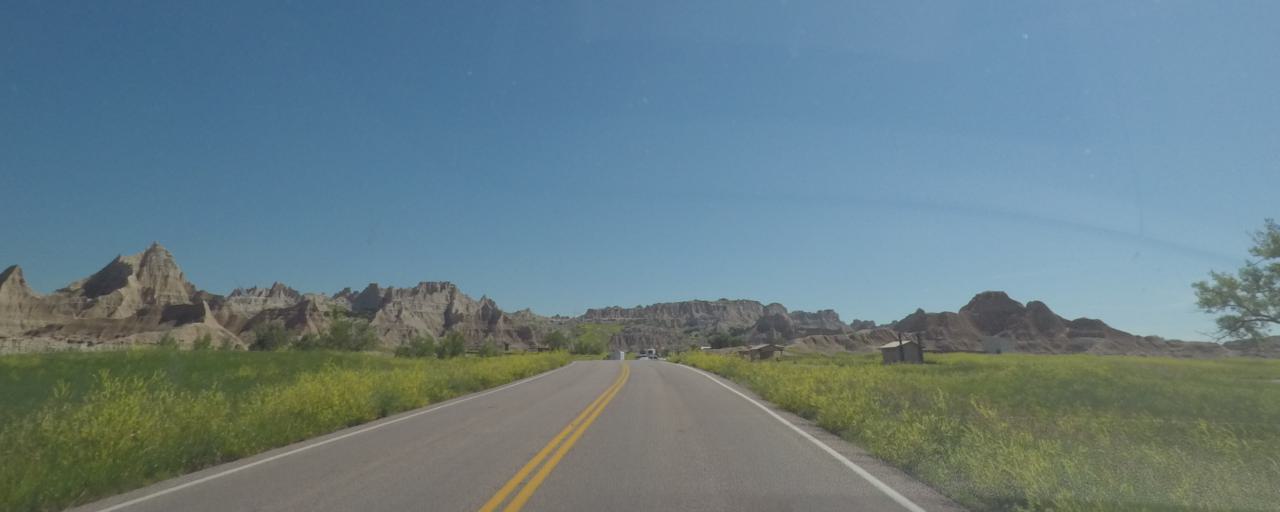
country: US
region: South Dakota
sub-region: Haakon County
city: Philip
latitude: 43.7462
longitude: -101.9491
